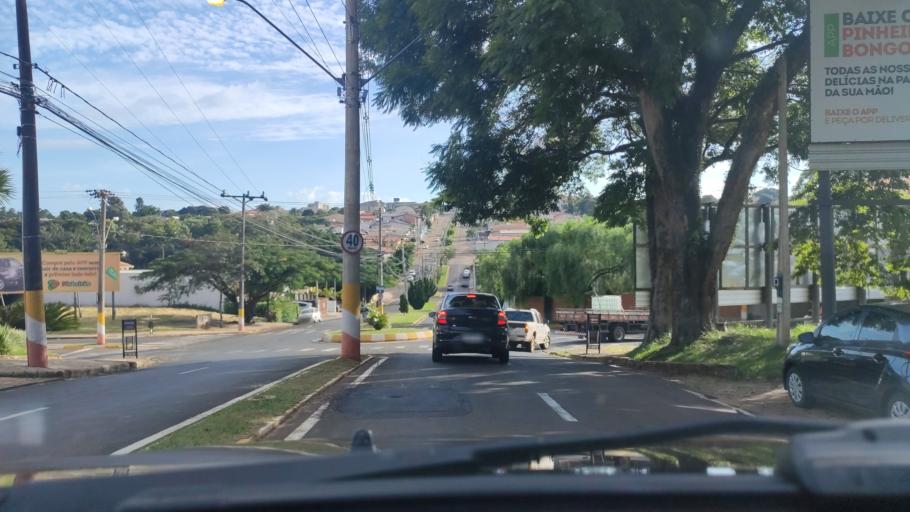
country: BR
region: Sao Paulo
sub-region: Avare
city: Avare
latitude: -23.0943
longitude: -48.9341
